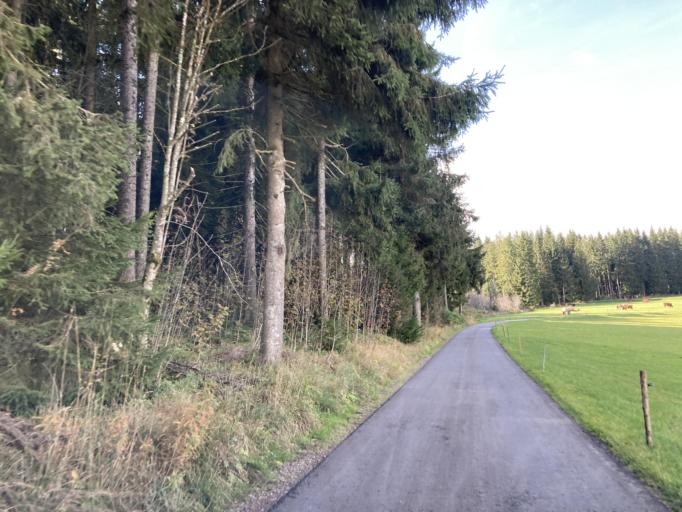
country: DE
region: Baden-Wuerttemberg
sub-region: Freiburg Region
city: Vohrenbach
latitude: 48.0968
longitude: 8.2781
